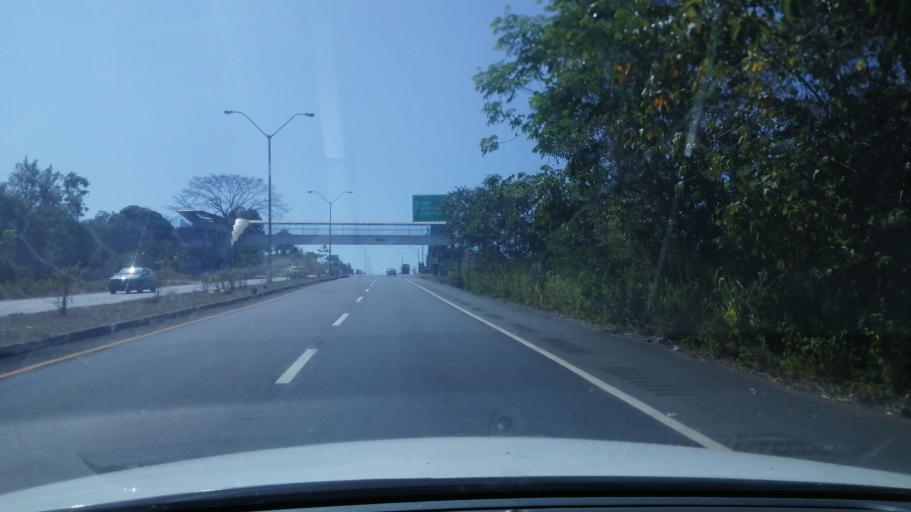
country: PA
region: Chiriqui
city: San Felix
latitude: 8.2775
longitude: -81.8701
